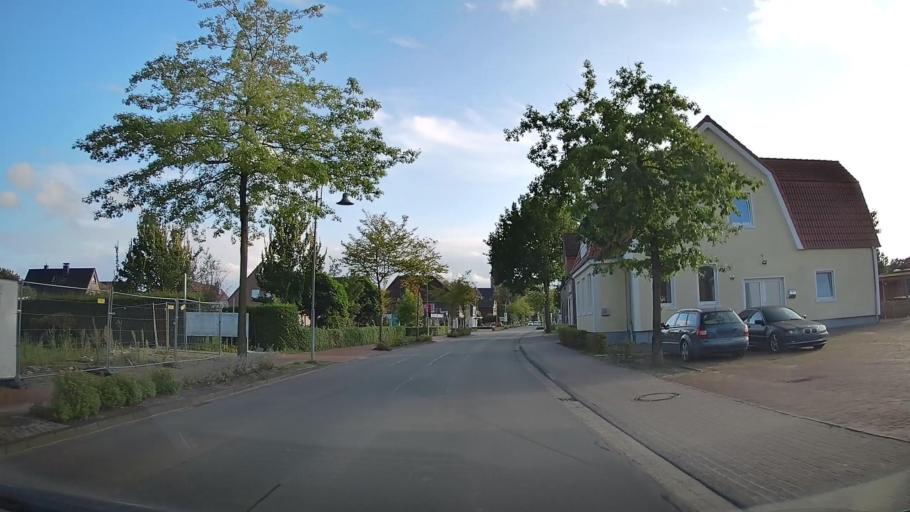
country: DE
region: Lower Saxony
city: Ostrhauderfehn
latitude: 53.1282
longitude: 7.6675
